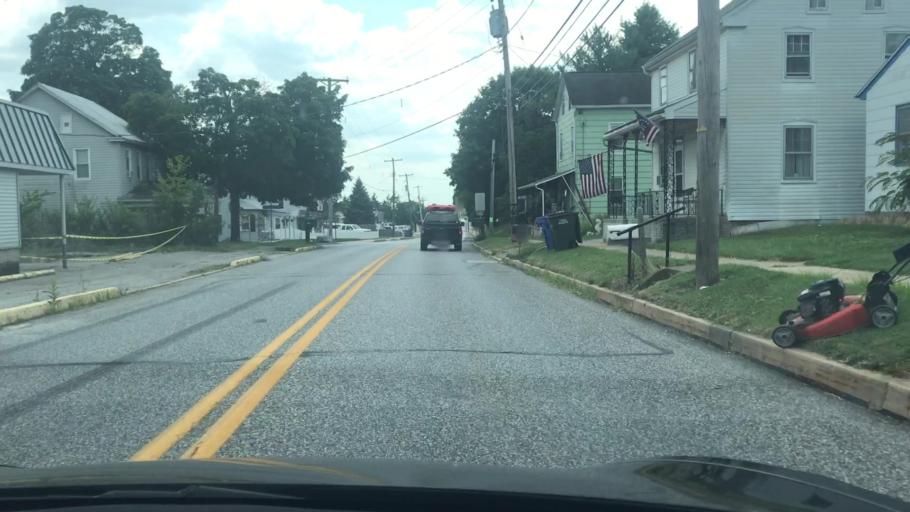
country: US
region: Pennsylvania
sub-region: York County
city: Manchester
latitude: 40.0886
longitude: -76.7626
